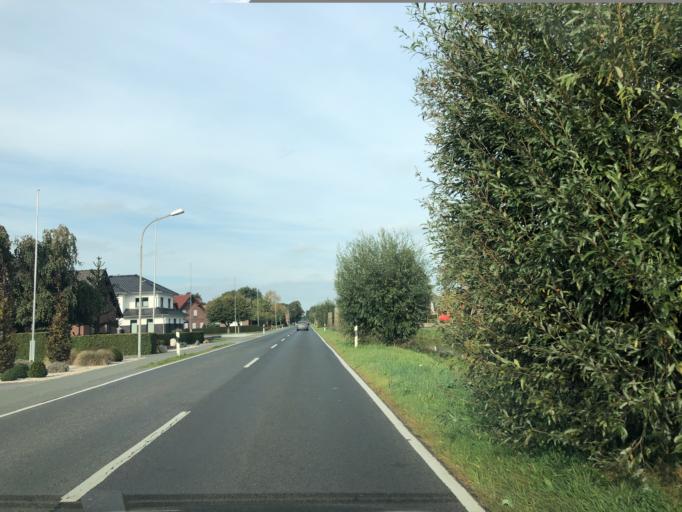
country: DE
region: Lower Saxony
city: Surwold
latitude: 53.0142
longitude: 7.4874
